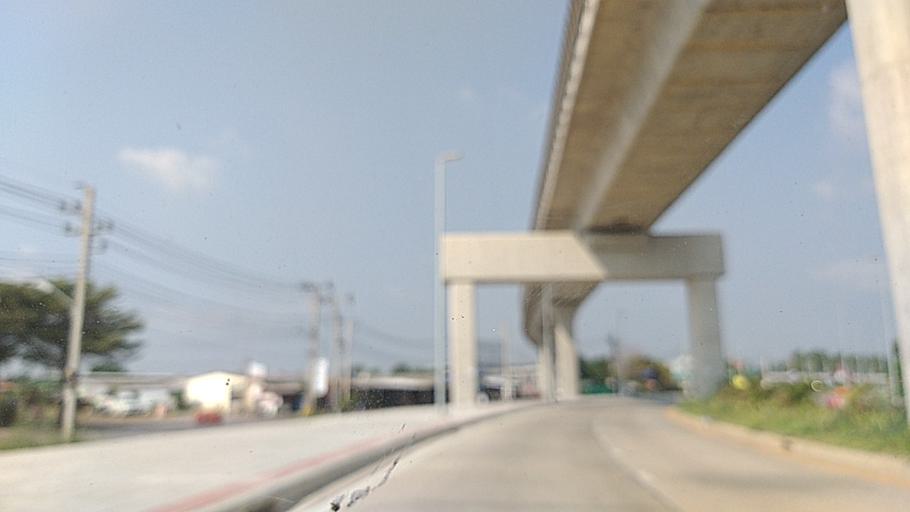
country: TH
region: Bangkok
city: Sai Mai
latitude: 13.9279
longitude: 100.6303
